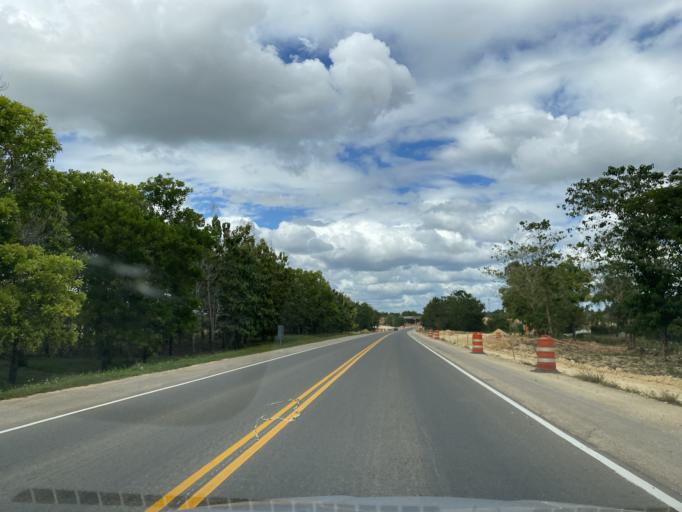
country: DO
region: Santo Domingo
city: Guerra
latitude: 18.5567
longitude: -69.7663
